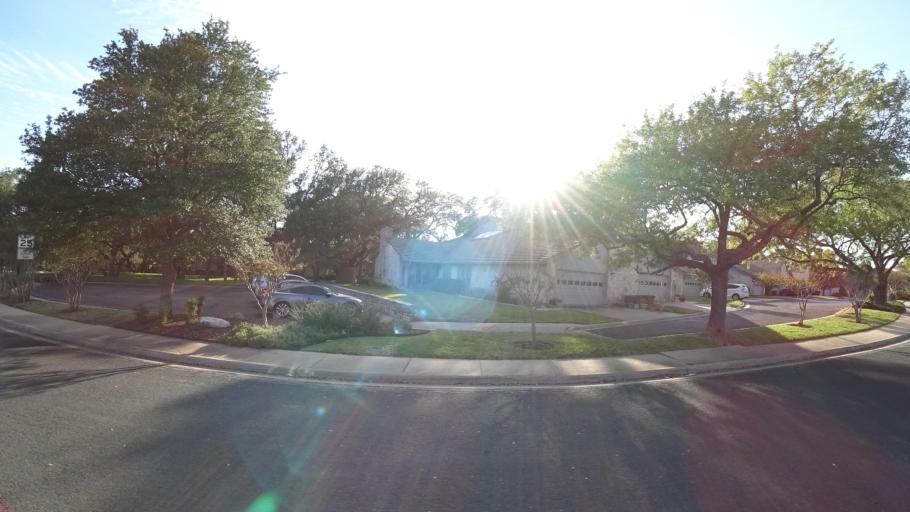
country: US
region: Texas
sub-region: Williamson County
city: Anderson Mill
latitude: 30.4440
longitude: -97.8042
